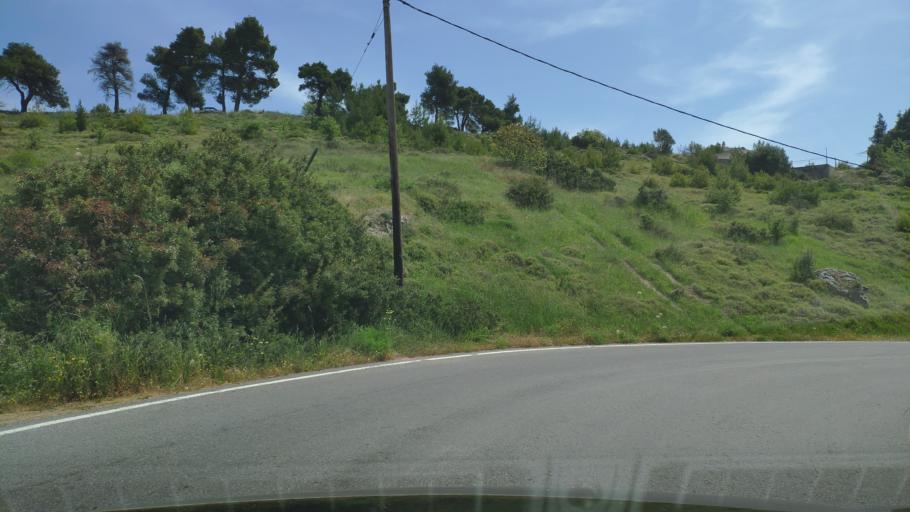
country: GR
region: Attica
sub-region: Nomarchia Anatolikis Attikis
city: Varnavas
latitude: 38.2221
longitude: 23.9272
